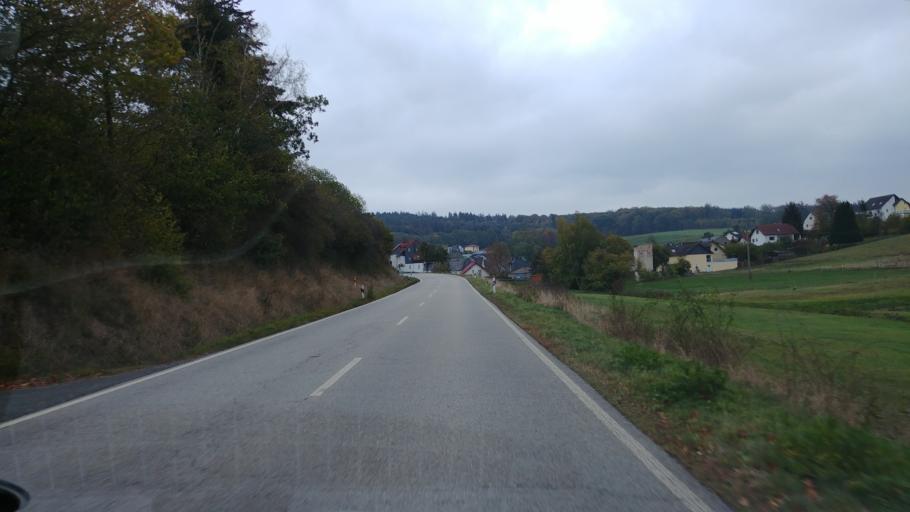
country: DE
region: Hesse
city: Taunusstein
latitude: 50.2077
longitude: 8.1876
